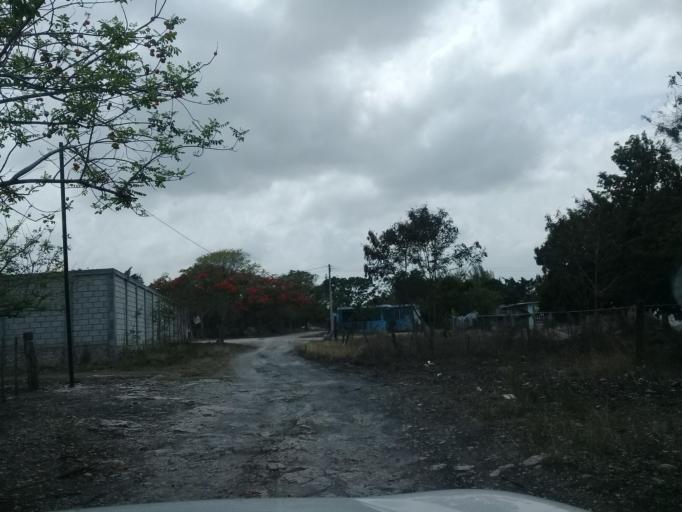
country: MX
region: Veracruz
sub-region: Emiliano Zapata
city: Plan del Rio
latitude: 19.3571
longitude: -96.6597
